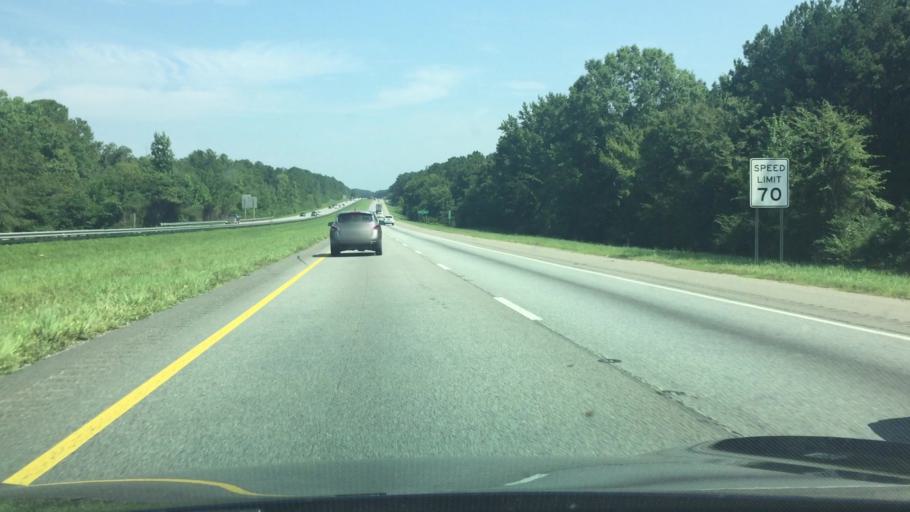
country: US
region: Alabama
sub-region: Shelby County
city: Calera
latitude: 33.1111
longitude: -86.7401
